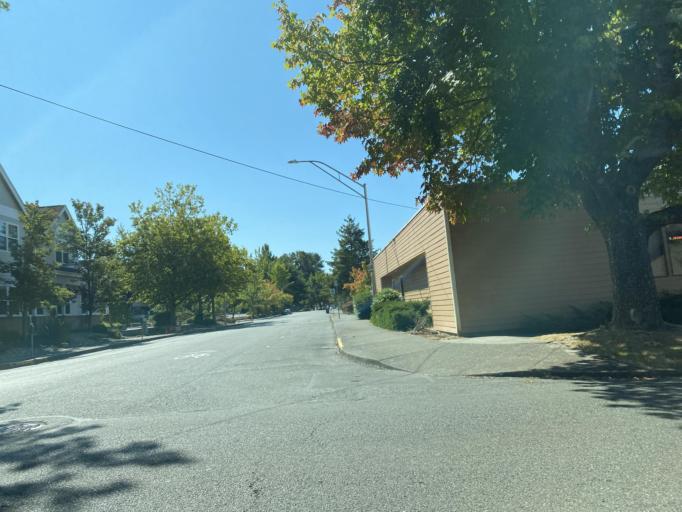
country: US
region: Washington
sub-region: Thurston County
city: Olympia
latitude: 47.0439
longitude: -122.8911
